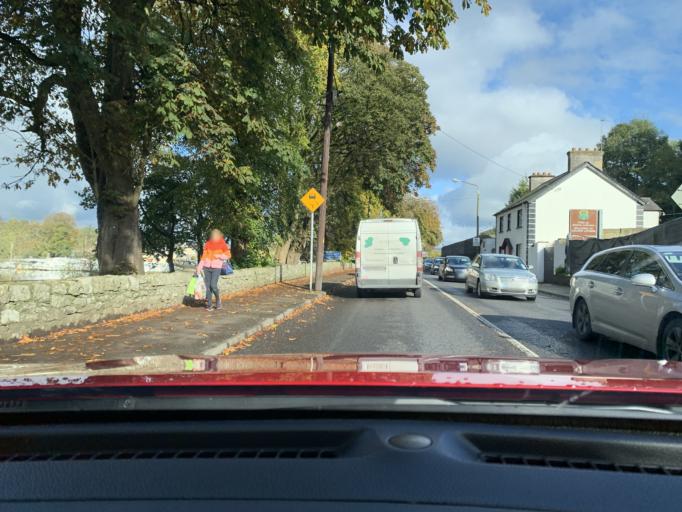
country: IE
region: Connaught
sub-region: County Leitrim
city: Carrick-on-Shannon
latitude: 53.9420
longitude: -8.0981
